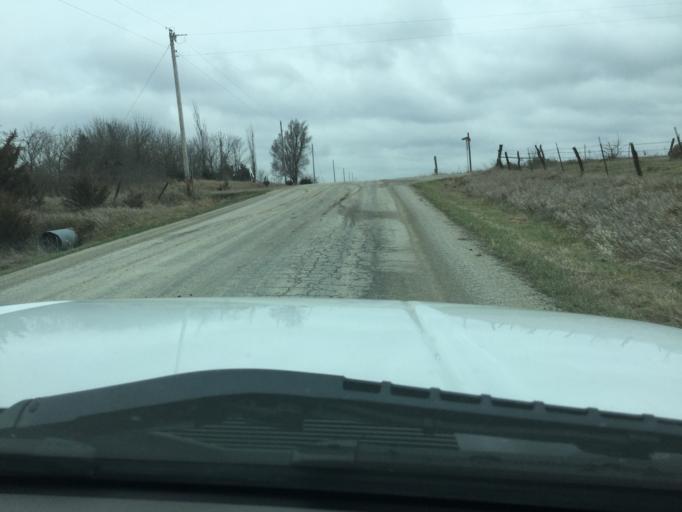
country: US
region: Kansas
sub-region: Nemaha County
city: Sabetha
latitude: 39.7981
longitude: -95.7704
